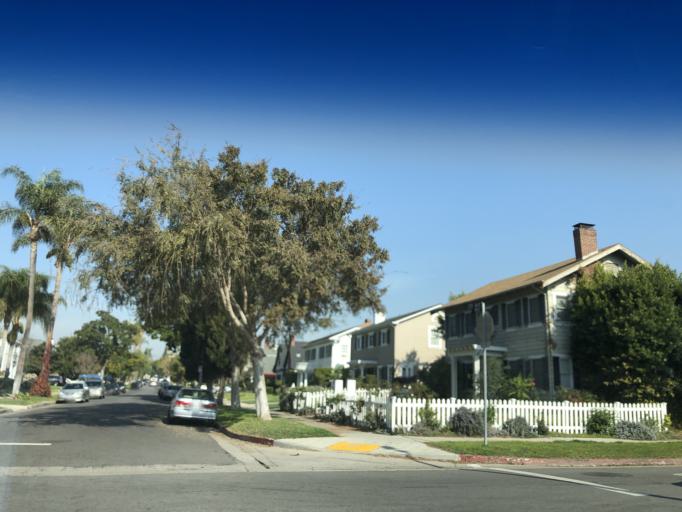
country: US
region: California
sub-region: Los Angeles County
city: Hollywood
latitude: 34.0558
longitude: -118.3165
